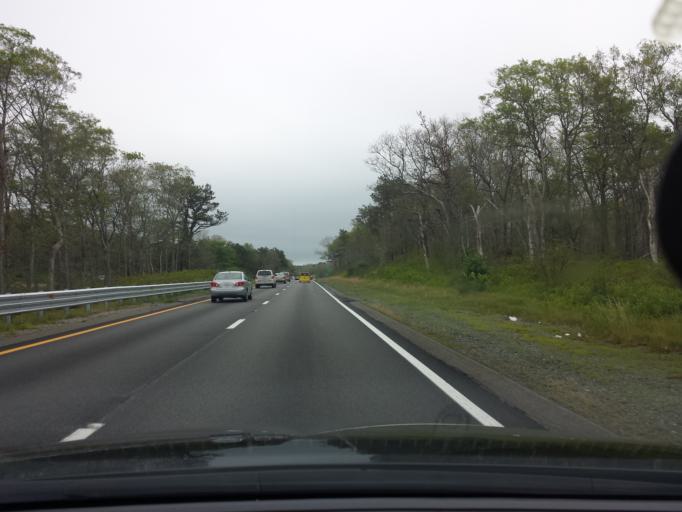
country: US
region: Massachusetts
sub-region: Barnstable County
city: West Barnstable
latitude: 41.7124
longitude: -70.4142
